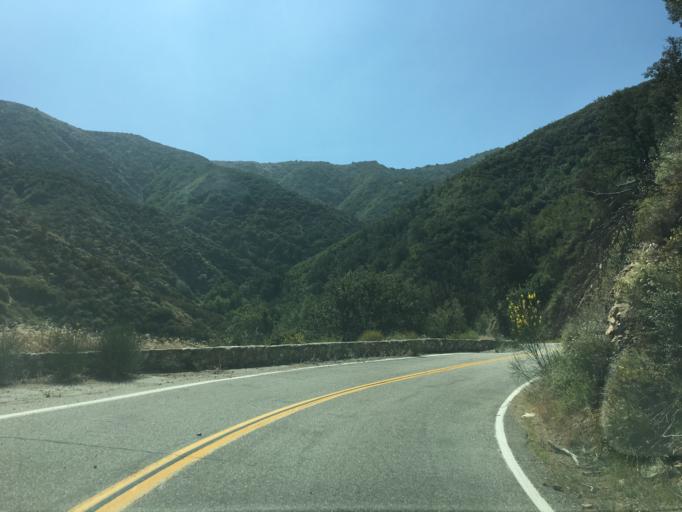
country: US
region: California
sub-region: Los Angeles County
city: Glendora
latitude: 34.2168
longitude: -117.7903
